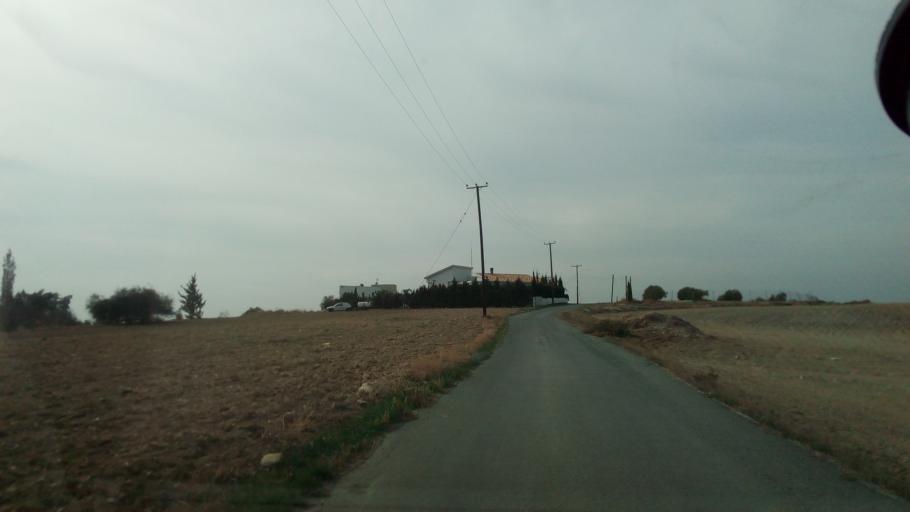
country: CY
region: Larnaka
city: Aradippou
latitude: 34.9558
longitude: 33.5762
